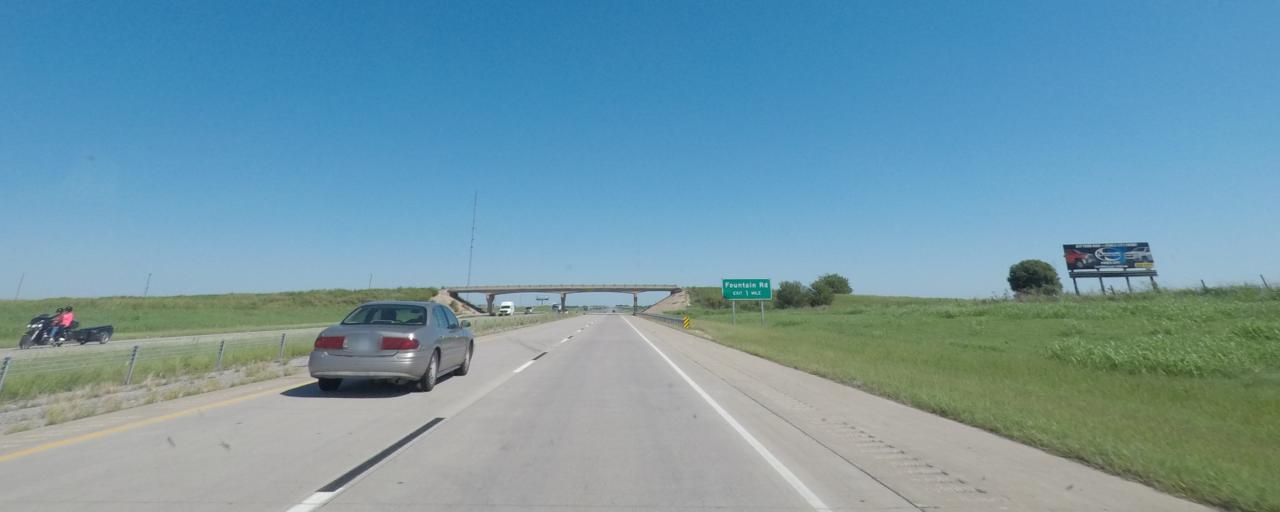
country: US
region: Oklahoma
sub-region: Kay County
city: Tonkawa
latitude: 36.6358
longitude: -97.3457
